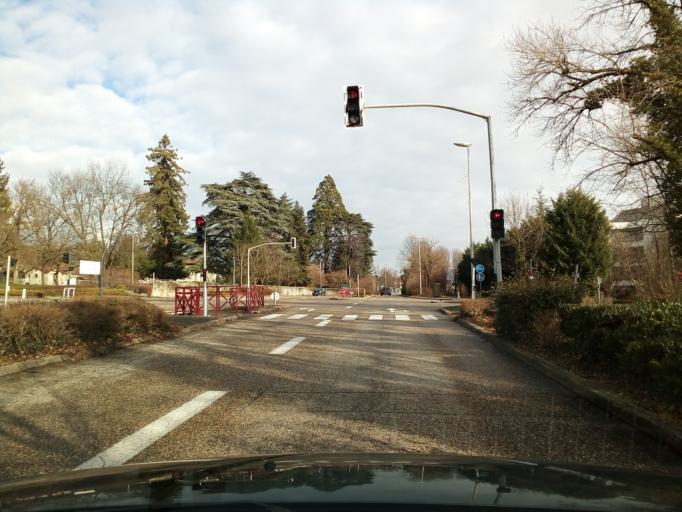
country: FR
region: Rhone-Alpes
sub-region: Departement de l'Isere
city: Corenc
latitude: 45.2133
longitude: 5.7772
